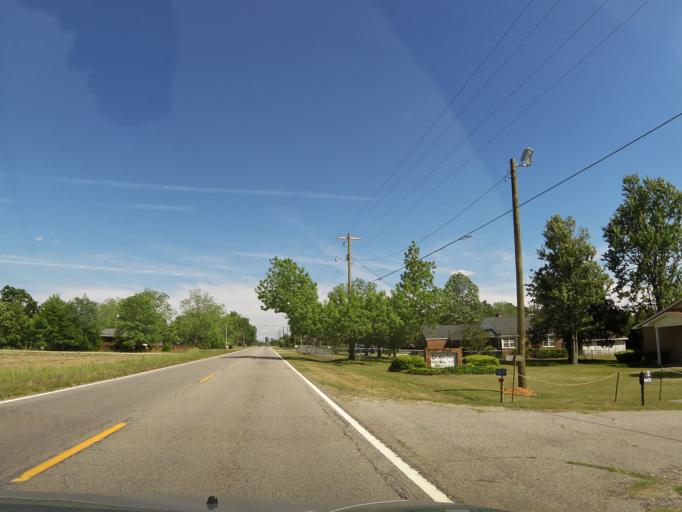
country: US
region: South Carolina
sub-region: Barnwell County
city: Williston
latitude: 33.4080
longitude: -81.4463
